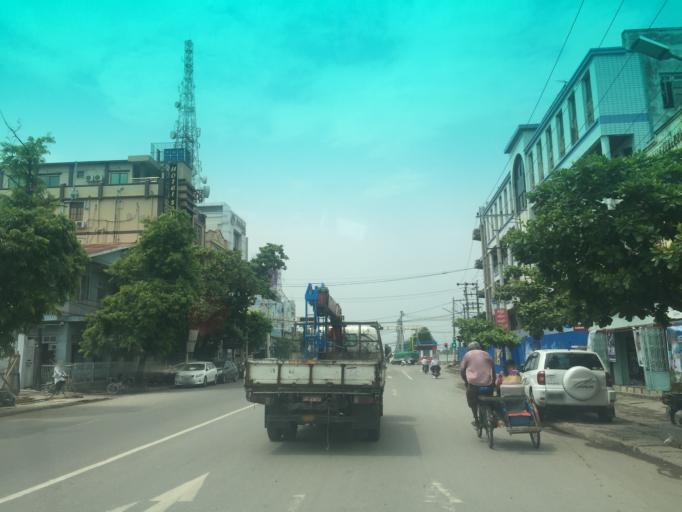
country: MM
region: Mandalay
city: Mandalay
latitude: 21.9823
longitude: 96.0844
